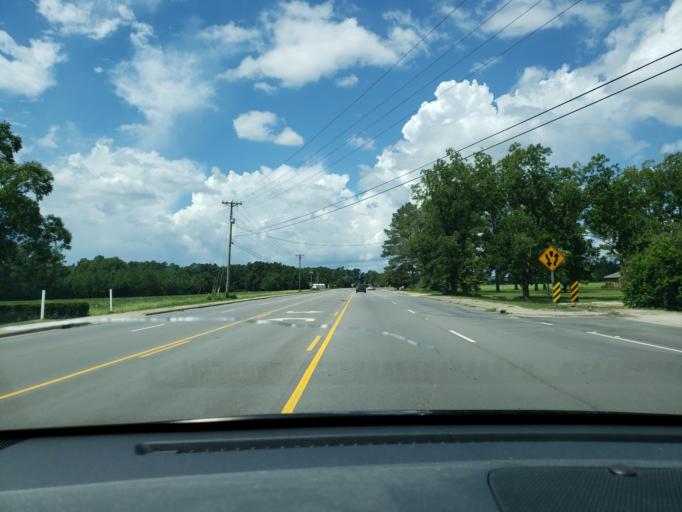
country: US
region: North Carolina
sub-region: Robeson County
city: Saint Pauls
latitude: 34.7362
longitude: -78.7958
